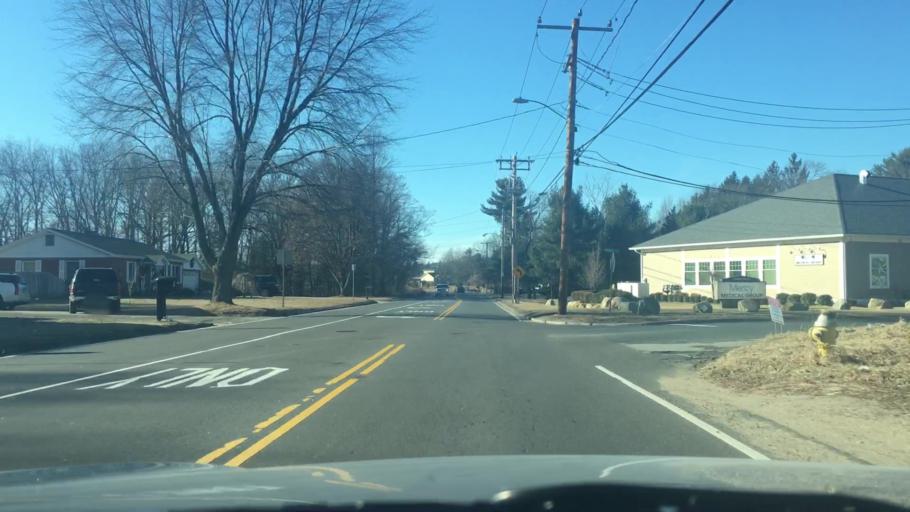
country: US
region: Massachusetts
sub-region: Hampden County
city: Ludlow
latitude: 42.1822
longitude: -72.5065
